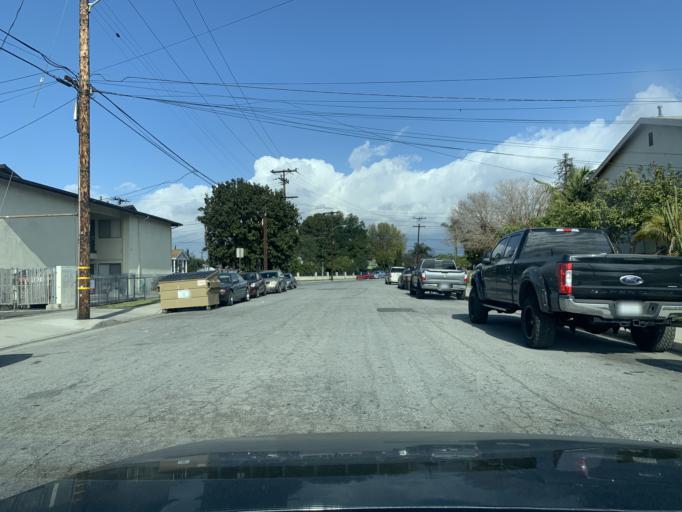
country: US
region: California
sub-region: Los Angeles County
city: South El Monte
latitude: 34.0644
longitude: -118.0543
